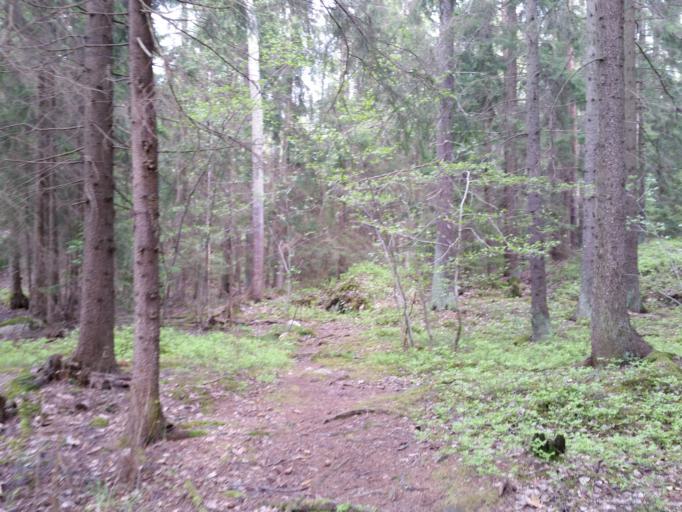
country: SE
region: Stockholm
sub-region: Sollentuna Kommun
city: Sollentuna
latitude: 59.4606
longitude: 17.9521
